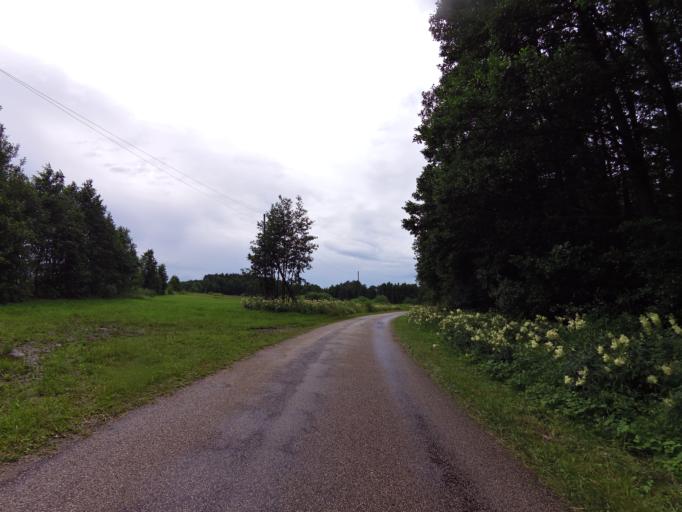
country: EE
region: Laeaene
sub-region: Vormsi vald
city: Hullo
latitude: 58.9982
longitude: 23.3428
